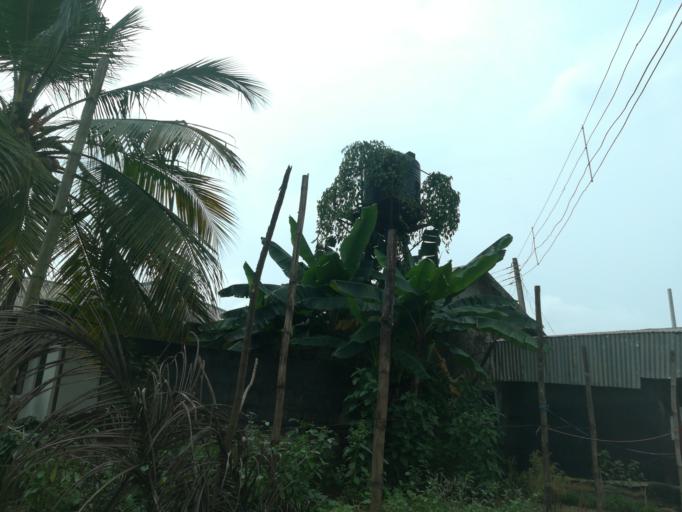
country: NG
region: Rivers
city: Port Harcourt
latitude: 4.8934
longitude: 6.9949
